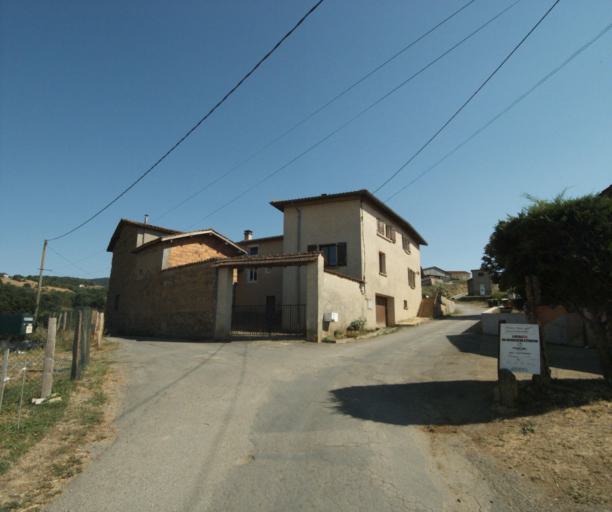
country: FR
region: Rhone-Alpes
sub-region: Departement du Rhone
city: Courzieu
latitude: 45.7590
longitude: 4.5715
